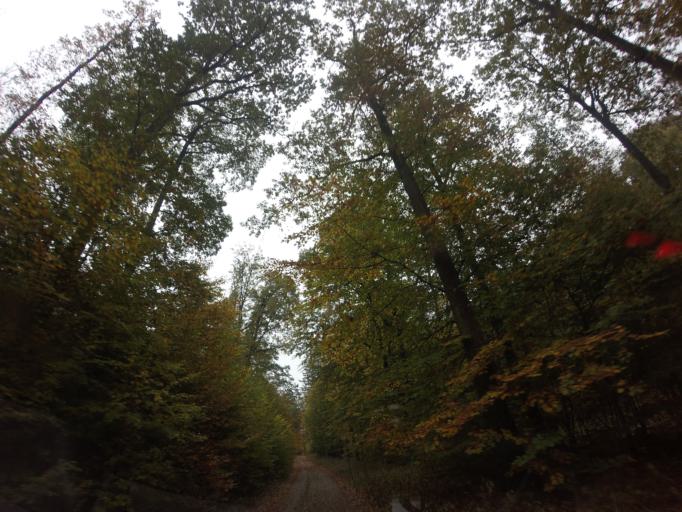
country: PL
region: West Pomeranian Voivodeship
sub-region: Powiat choszczenski
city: Krzecin
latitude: 53.0210
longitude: 15.4998
